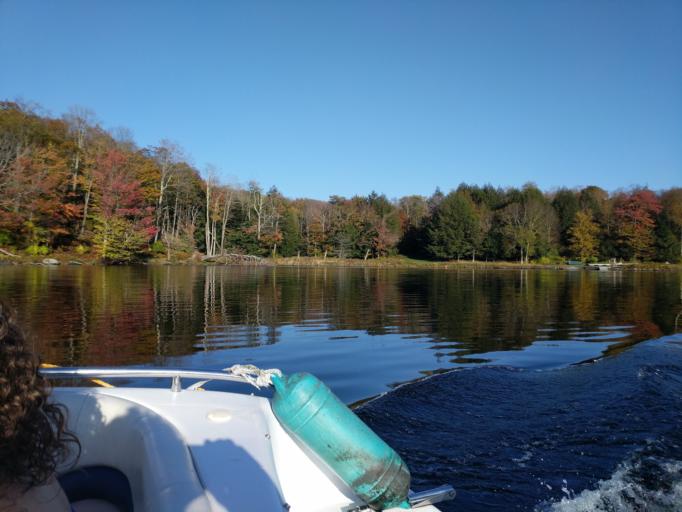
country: US
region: New York
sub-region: Sullivan County
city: Livingston Manor
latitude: 41.8827
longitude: -74.9718
